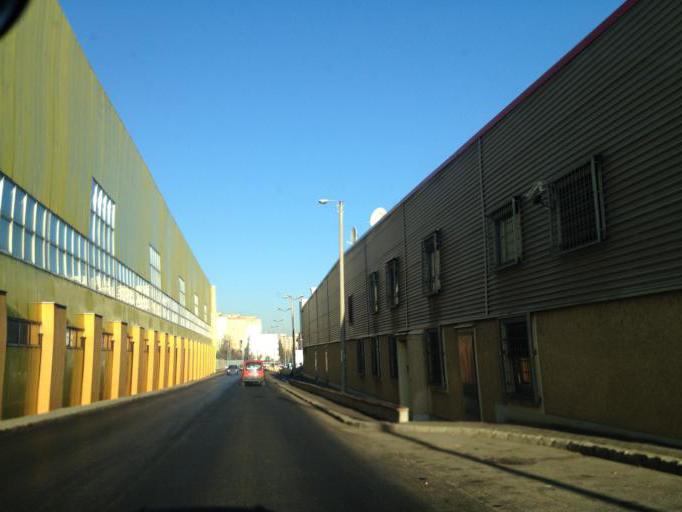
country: RO
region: Brasov
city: Brasov
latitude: 45.6318
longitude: 25.6347
